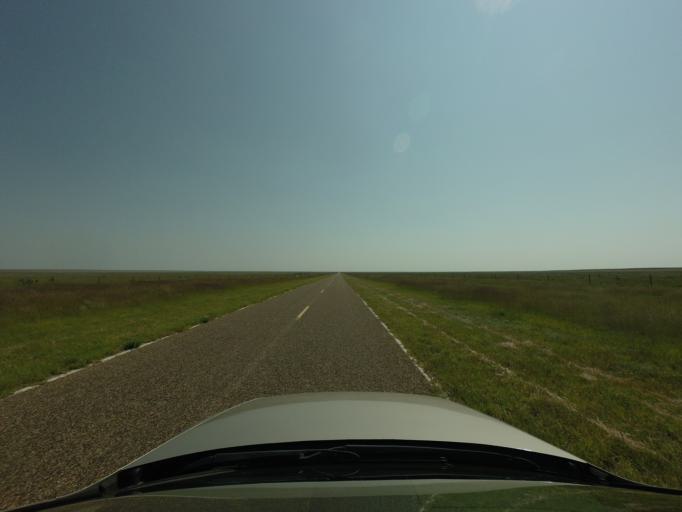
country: US
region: New Mexico
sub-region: Curry County
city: Cannon Air Force Base
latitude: 34.6334
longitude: -103.4886
